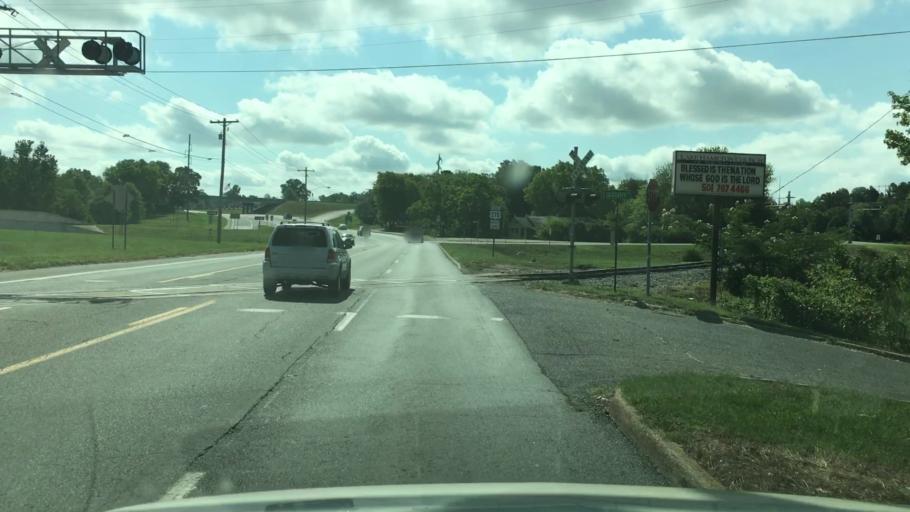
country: US
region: Arkansas
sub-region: Garland County
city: Piney
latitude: 34.4934
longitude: -93.1161
